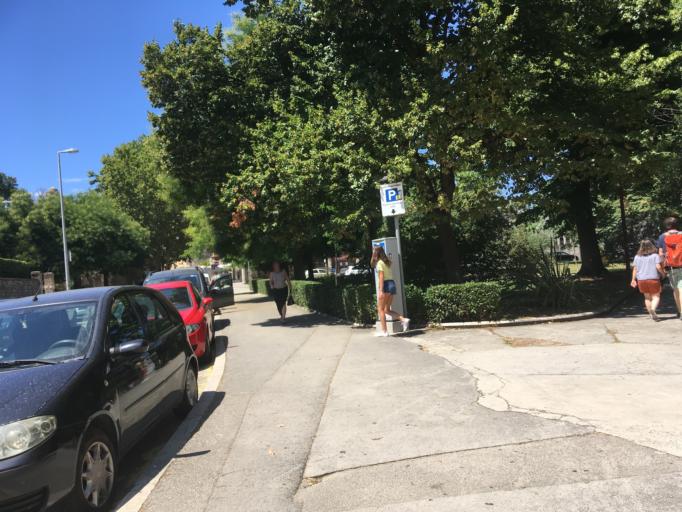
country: HR
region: Zadarska
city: Zadar
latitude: 44.1127
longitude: 15.2308
